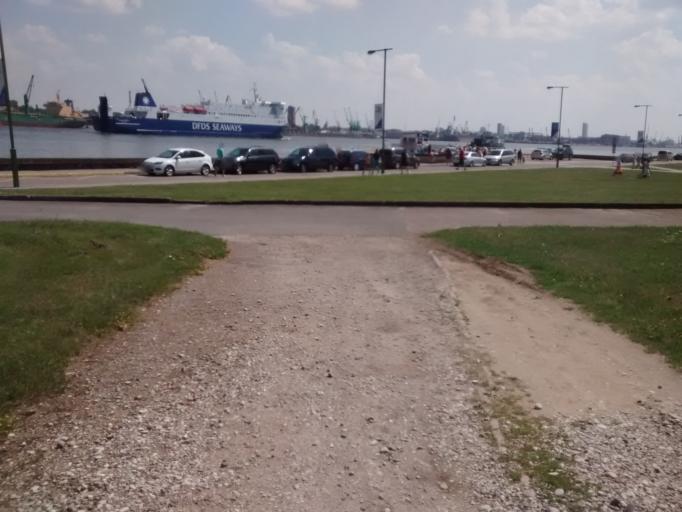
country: LT
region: Klaipedos apskritis
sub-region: Klaipeda
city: Klaipeda
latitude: 55.7159
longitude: 21.1029
